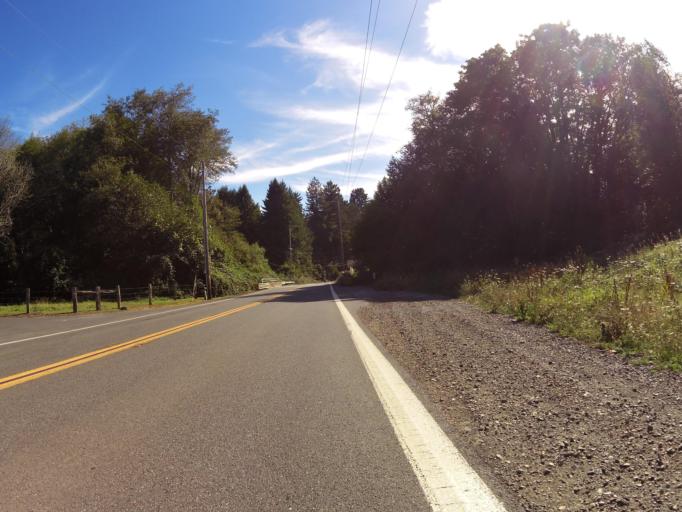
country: US
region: California
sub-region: Del Norte County
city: Bertsch-Oceanview
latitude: 41.8595
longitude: -124.1176
